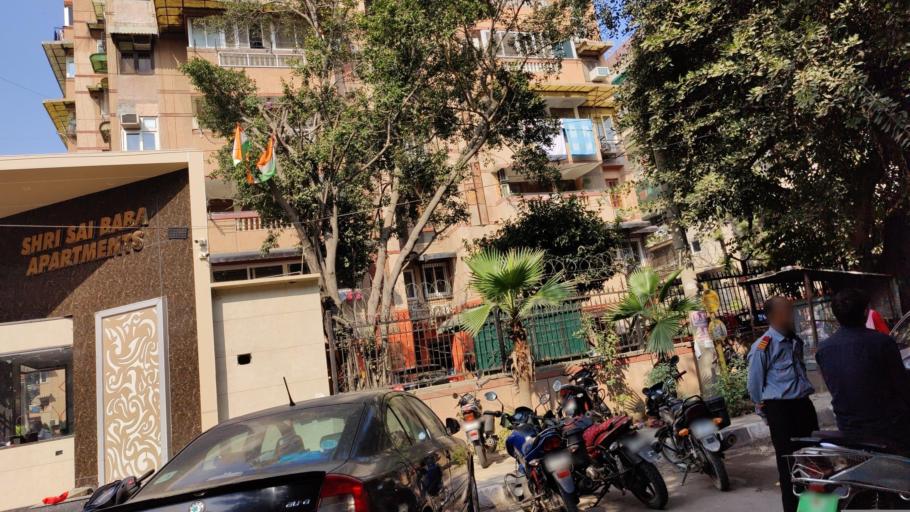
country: IN
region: NCT
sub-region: North West Delhi
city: Pitampura
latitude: 28.7093
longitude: 77.1254
